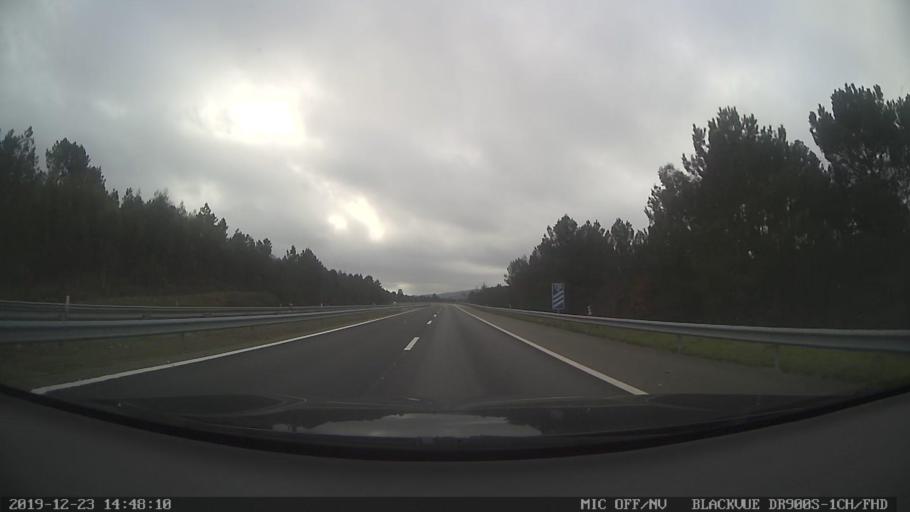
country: PT
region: Viseu
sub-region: Castro Daire
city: Castro Daire
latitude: 40.8716
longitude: -7.9251
